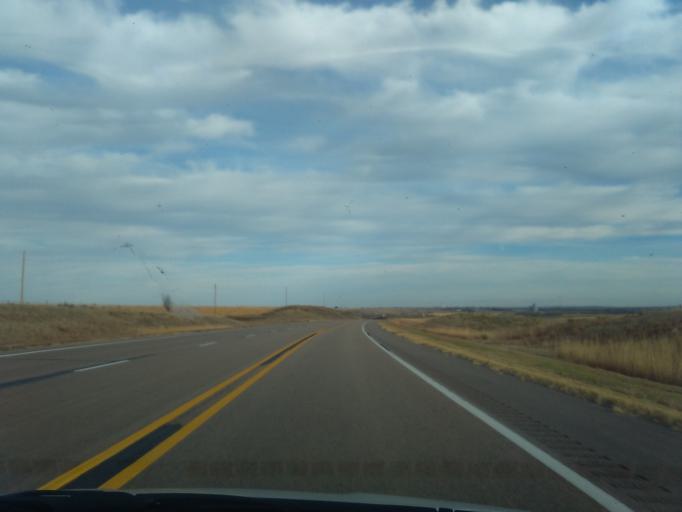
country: US
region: Nebraska
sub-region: Hitchcock County
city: Trenton
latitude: 40.2340
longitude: -100.9082
